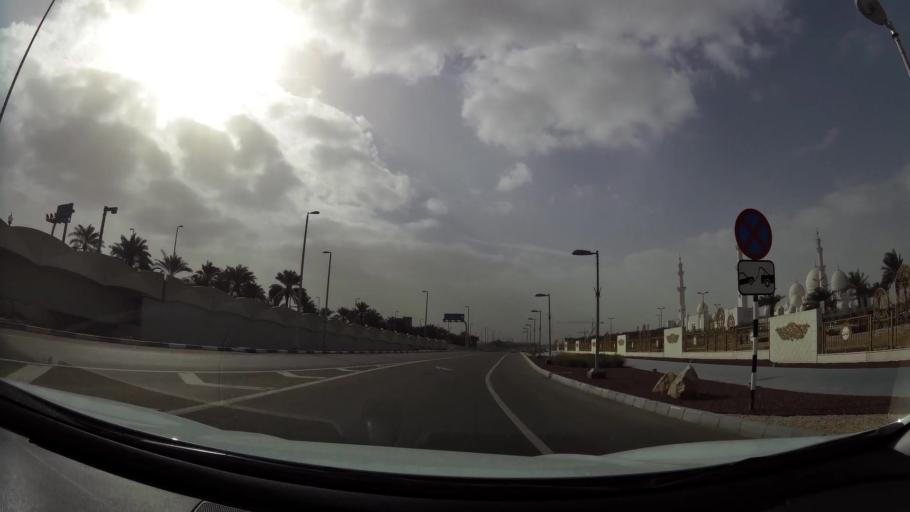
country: AE
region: Abu Dhabi
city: Abu Dhabi
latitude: 24.4167
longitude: 54.4774
